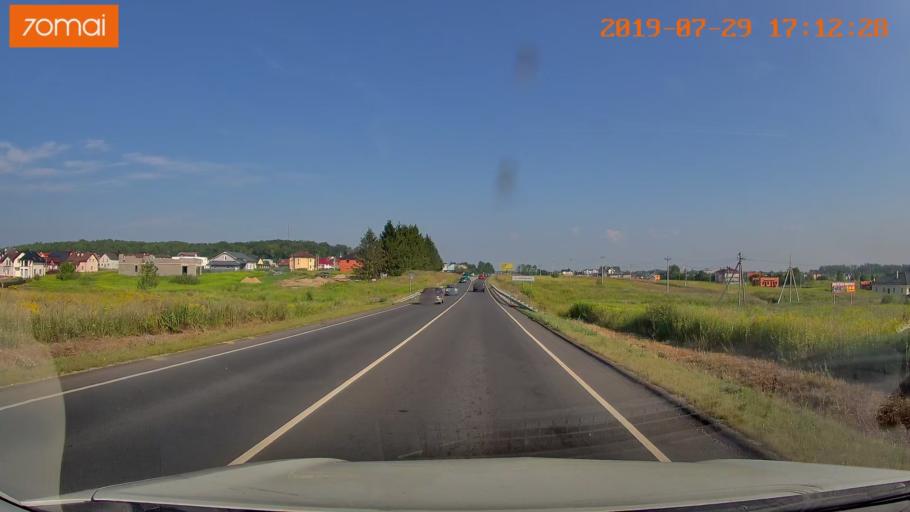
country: RU
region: Kaliningrad
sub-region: Gorod Kaliningrad
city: Kaliningrad
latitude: 54.7882
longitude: 20.3981
